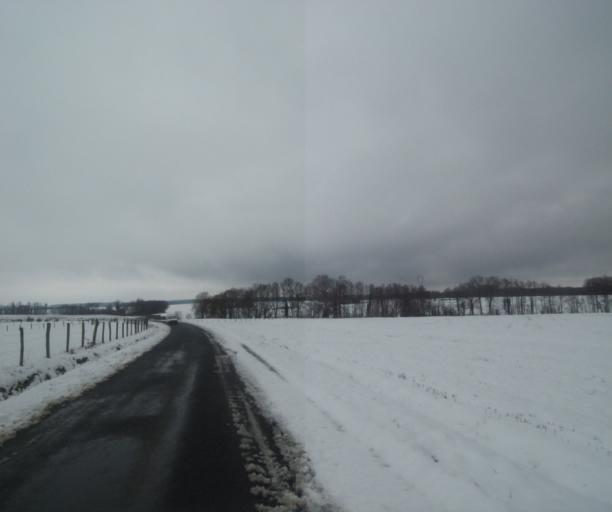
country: FR
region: Champagne-Ardenne
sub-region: Departement de la Haute-Marne
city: Laneuville-a-Remy
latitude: 48.5119
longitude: 4.8881
